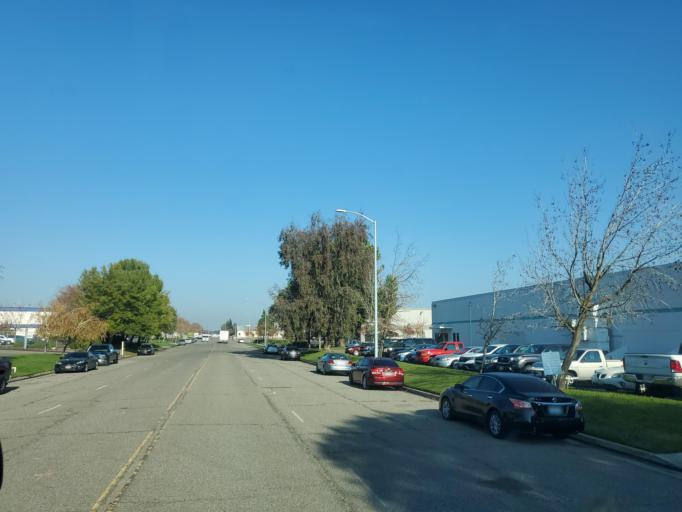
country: US
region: California
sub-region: San Joaquin County
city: French Camp
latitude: 37.8873
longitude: -121.2473
